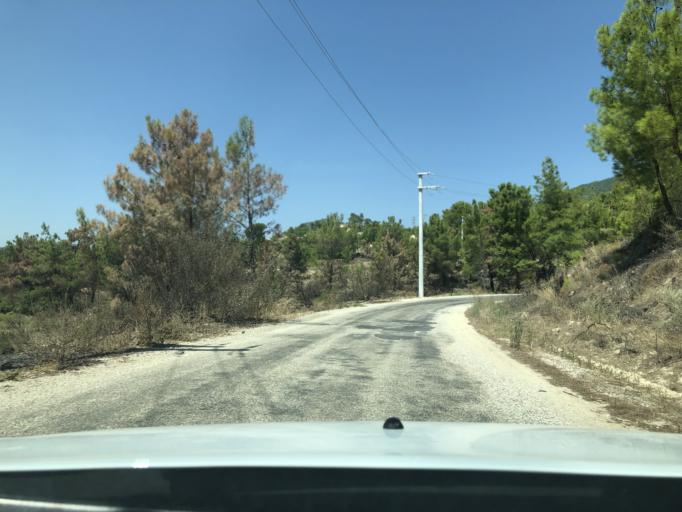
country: TR
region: Antalya
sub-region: Manavgat
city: Kizilagac
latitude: 36.8664
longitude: 31.5580
